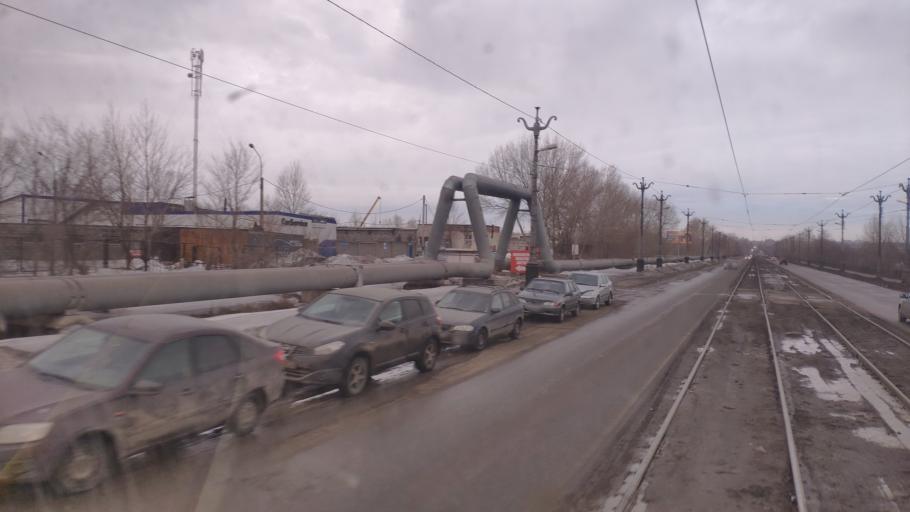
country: RU
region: Chelyabinsk
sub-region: Gorod Magnitogorsk
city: Magnitogorsk
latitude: 53.4222
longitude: 59.0261
